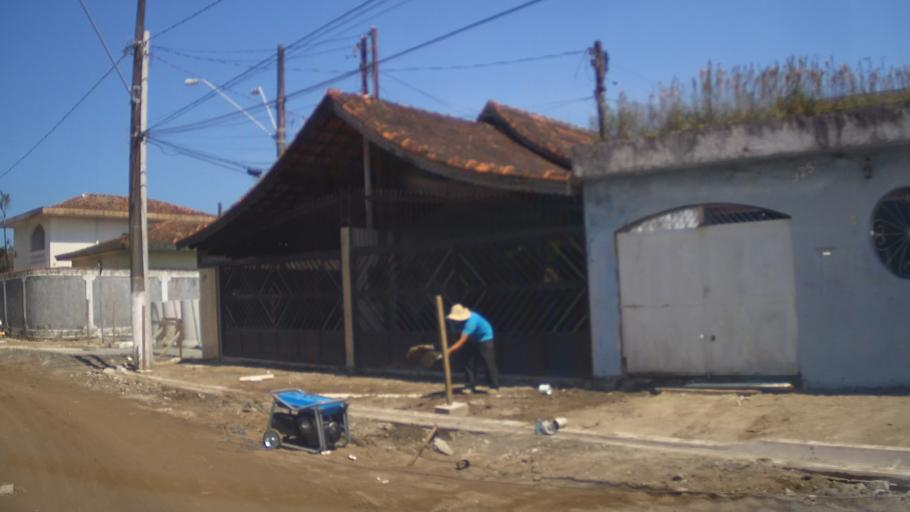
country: BR
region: Sao Paulo
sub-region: Praia Grande
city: Praia Grande
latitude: -24.0053
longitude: -46.4100
